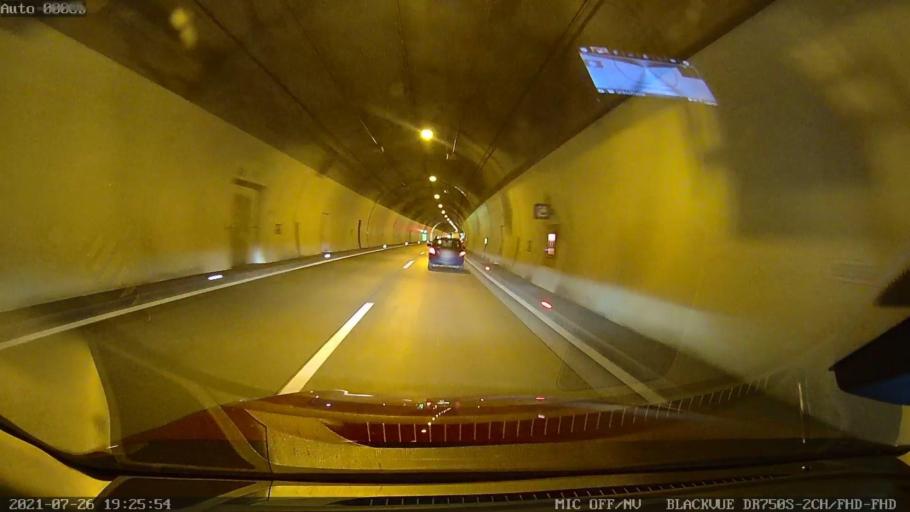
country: AT
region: Upper Austria
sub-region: Politischer Bezirk Kirchdorf an der Krems
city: Micheldorf in Oberoesterreich
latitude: 47.8594
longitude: 14.1542
